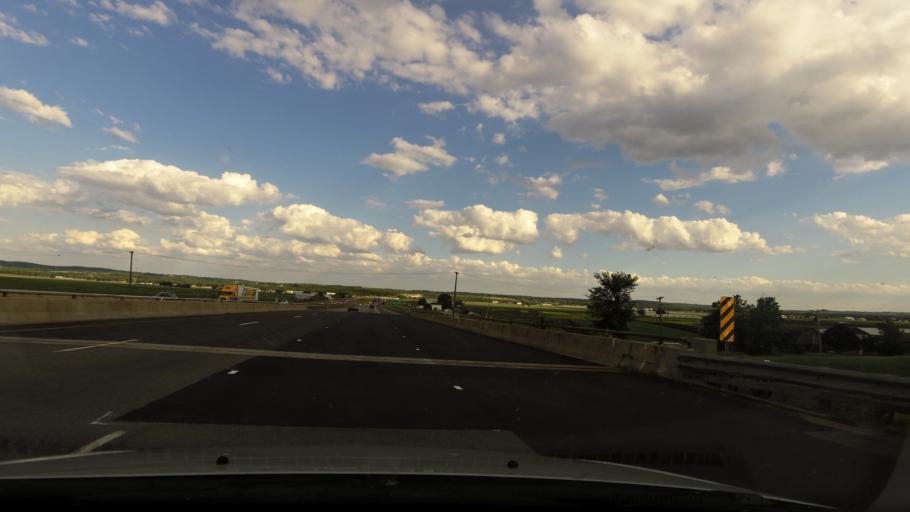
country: CA
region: Ontario
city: Bradford West Gwillimbury
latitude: 44.0530
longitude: -79.6100
